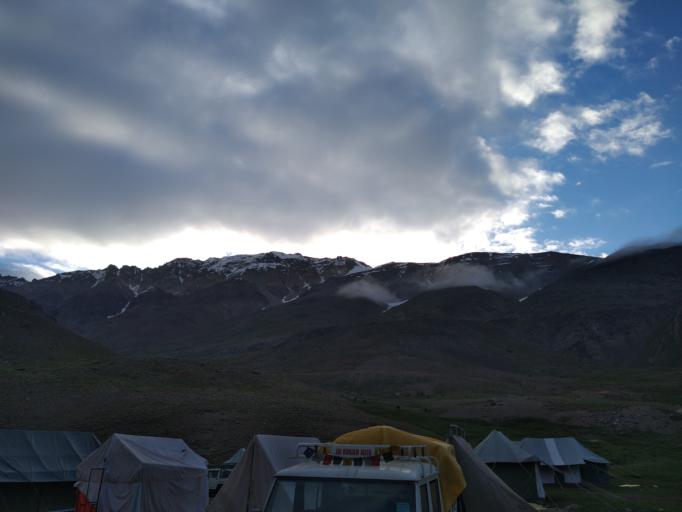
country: IN
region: Himachal Pradesh
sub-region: Kulu
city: Manali
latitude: 32.4510
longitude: 77.6107
